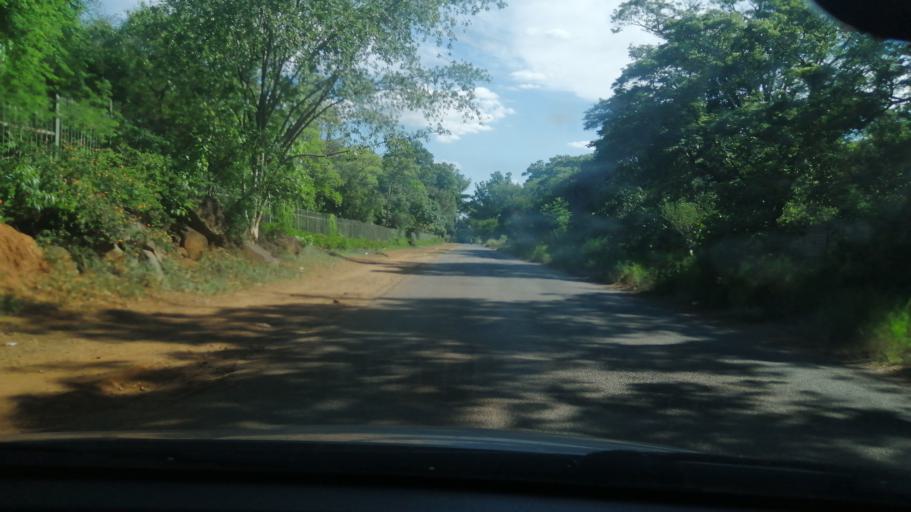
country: ZW
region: Harare
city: Harare
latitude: -17.7994
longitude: 31.0509
